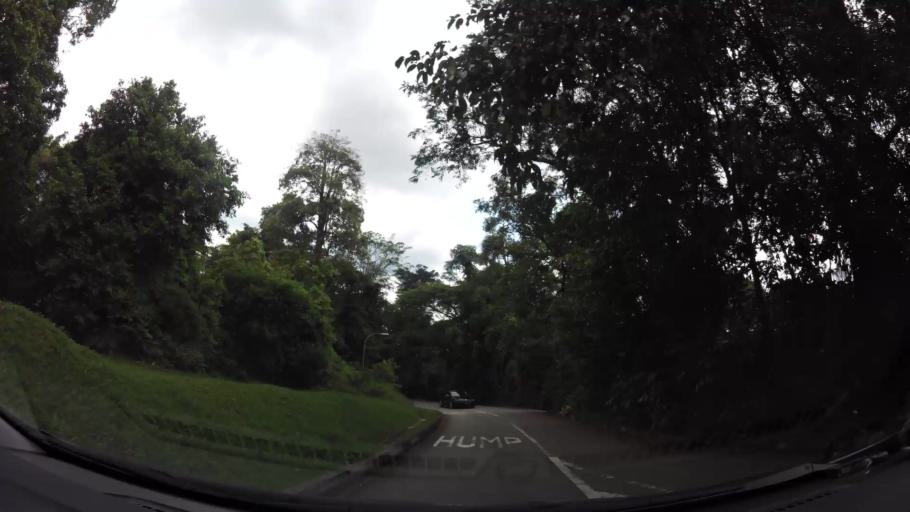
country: SG
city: Singapore
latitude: 1.2832
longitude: 103.7985
